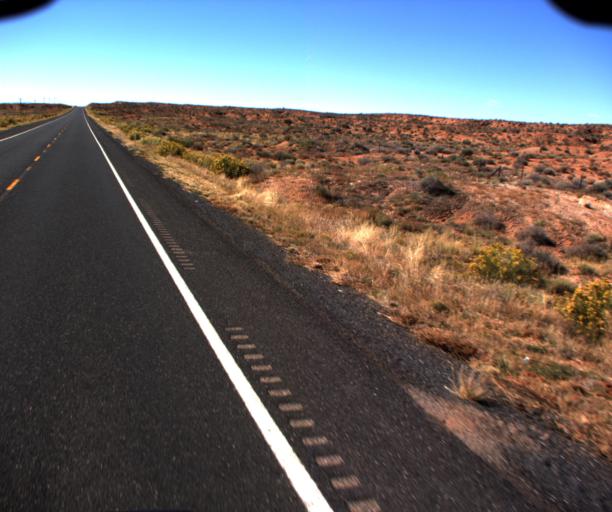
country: US
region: Arizona
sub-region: Coconino County
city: Fredonia
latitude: 36.9135
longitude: -112.5830
